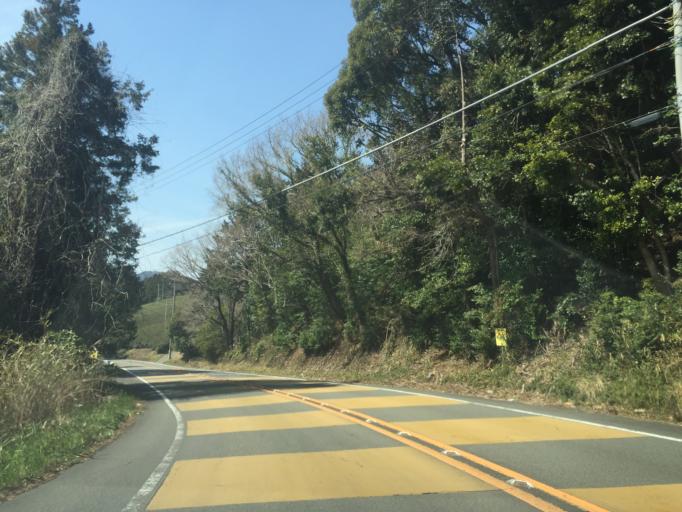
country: JP
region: Shizuoka
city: Kanaya
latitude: 34.8209
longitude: 138.1132
